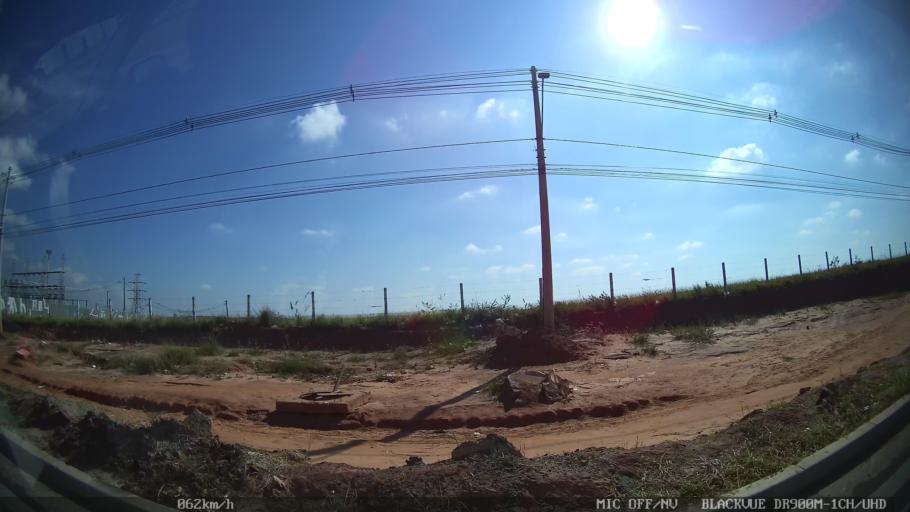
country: BR
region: Sao Paulo
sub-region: Campinas
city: Campinas
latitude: -22.9671
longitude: -47.1593
